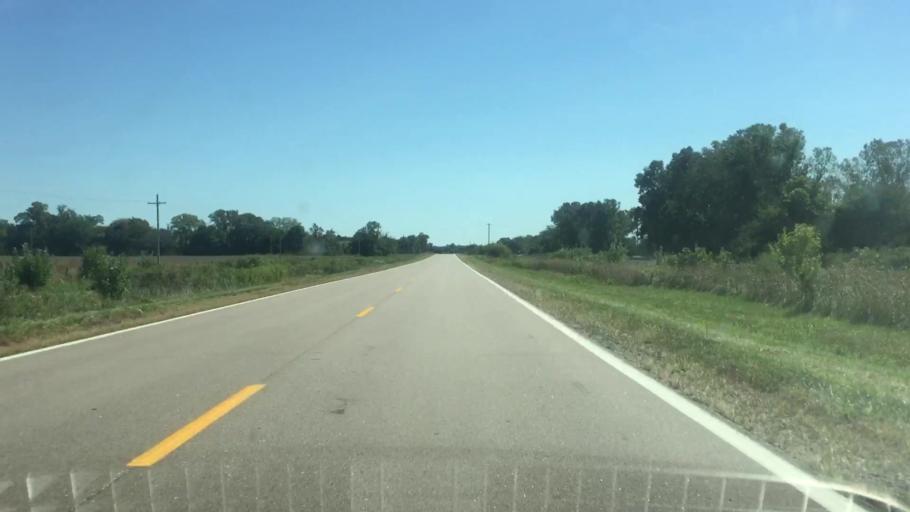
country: US
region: Nebraska
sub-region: Jefferson County
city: Fairbury
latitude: 40.0671
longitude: -97.0591
